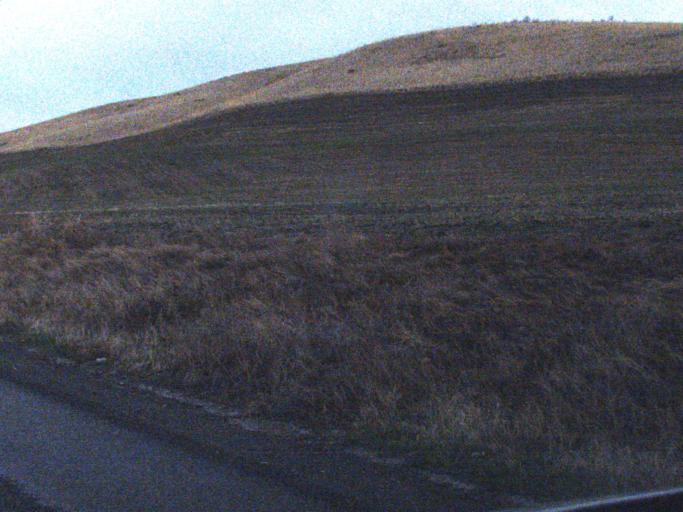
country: US
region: Washington
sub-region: Garfield County
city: Pomeroy
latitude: 46.5266
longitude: -117.8341
